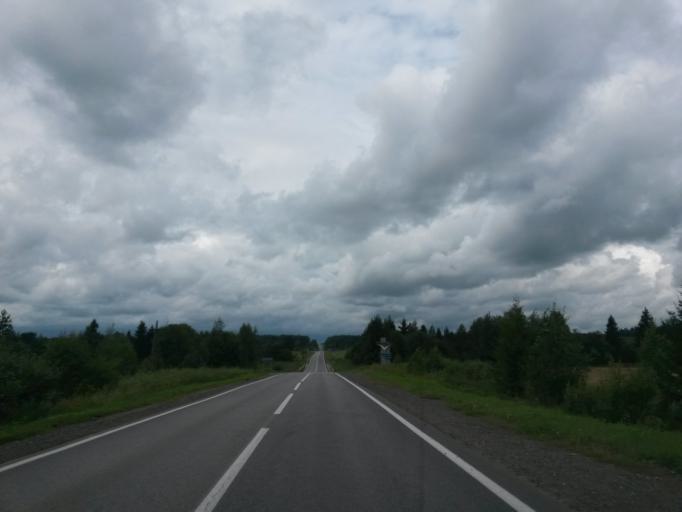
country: RU
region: Jaroslavl
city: Konstantinovskiy
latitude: 57.8103
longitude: 39.7337
